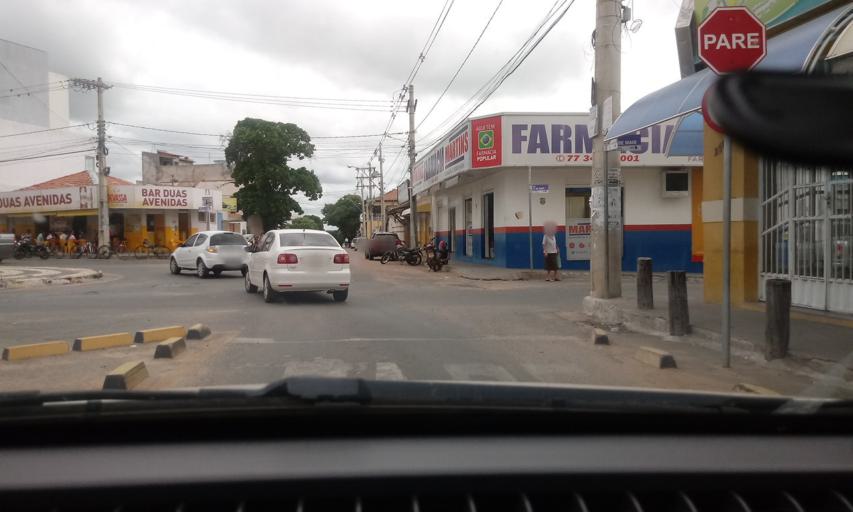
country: BR
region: Bahia
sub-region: Guanambi
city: Guanambi
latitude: -14.2197
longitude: -42.7796
